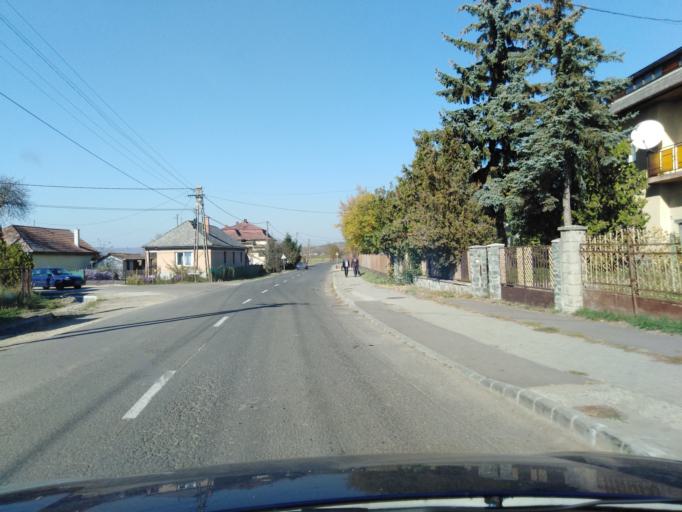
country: HU
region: Nograd
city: Karancskeszi
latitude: 48.1636
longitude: 19.6976
